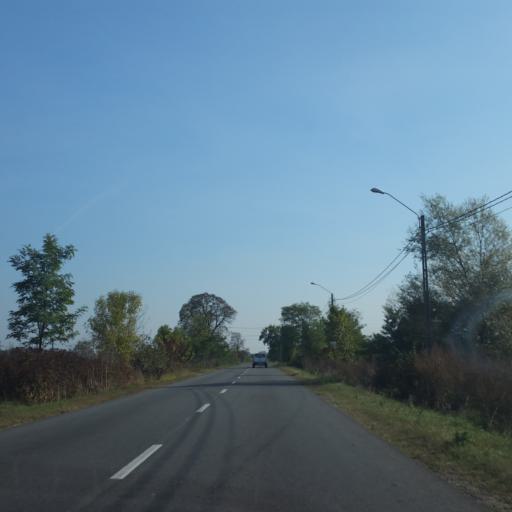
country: RO
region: Arges
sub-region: Comuna Merisani
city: Merisani
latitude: 44.9992
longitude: 24.7339
